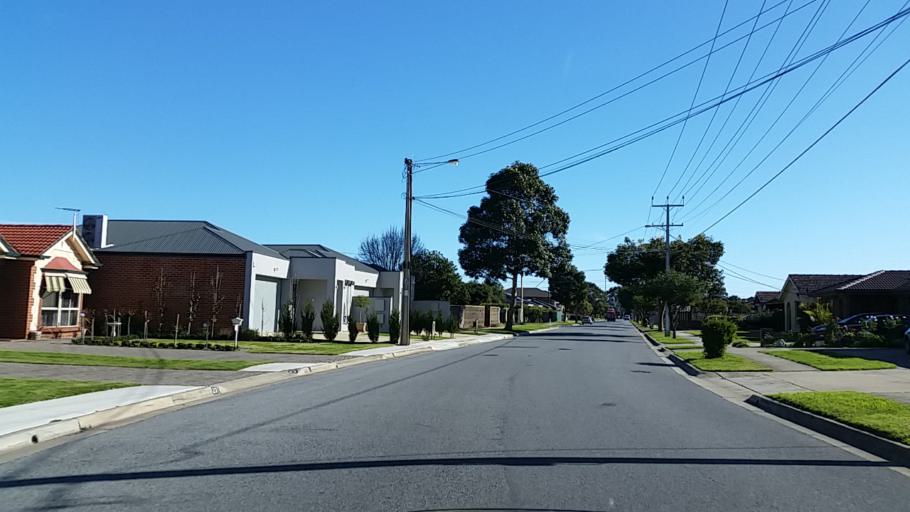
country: AU
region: South Australia
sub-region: Charles Sturt
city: Henley Beach
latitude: -34.9202
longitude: 138.5101
